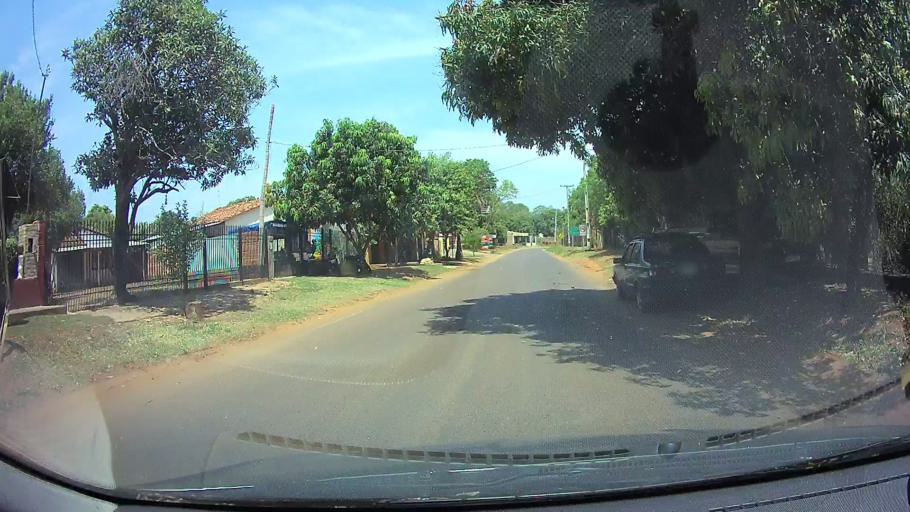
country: PY
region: Central
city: Ita
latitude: -25.4324
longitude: -57.3975
